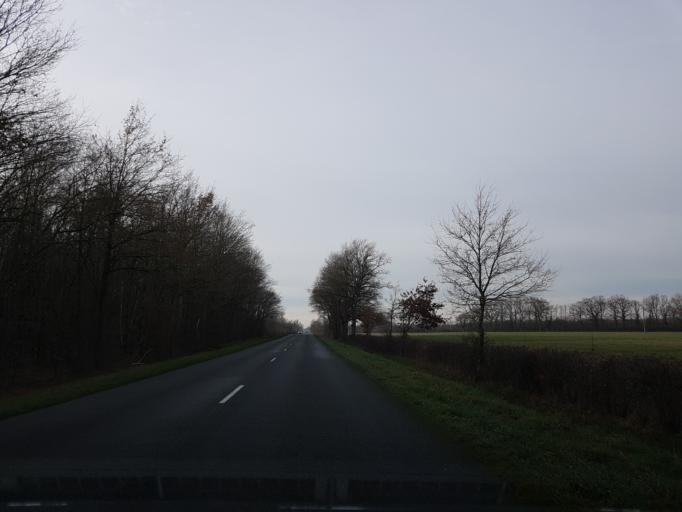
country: FR
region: Auvergne
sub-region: Departement de l'Allier
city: Lusigny
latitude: 46.5785
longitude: 3.4262
